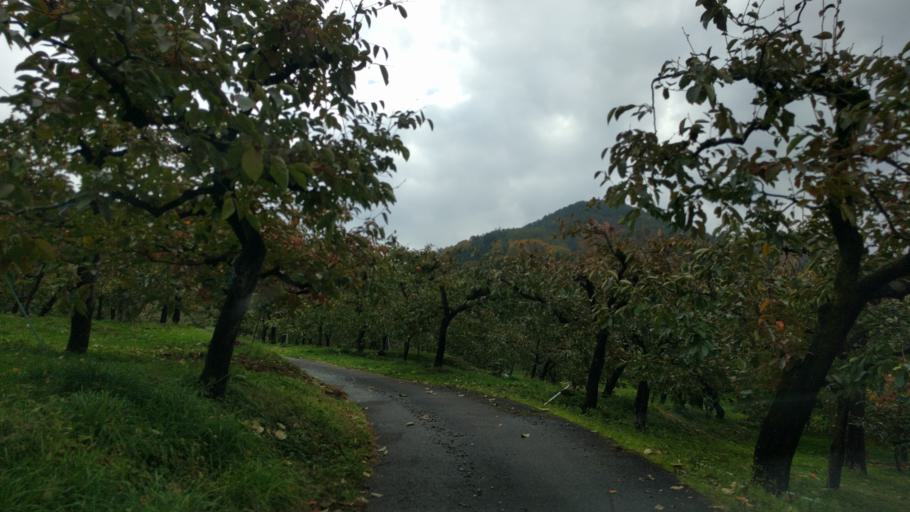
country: JP
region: Fukushima
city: Kitakata
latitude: 37.4595
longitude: 139.9366
